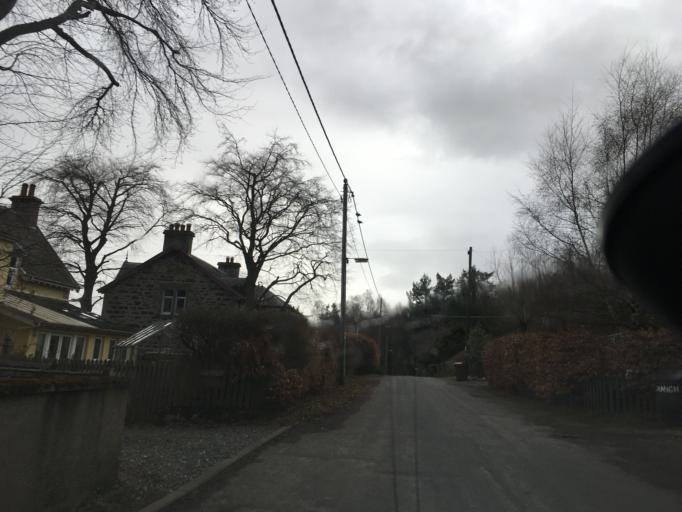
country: GB
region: Scotland
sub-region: Highland
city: Kingussie
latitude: 57.0825
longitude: -4.0557
